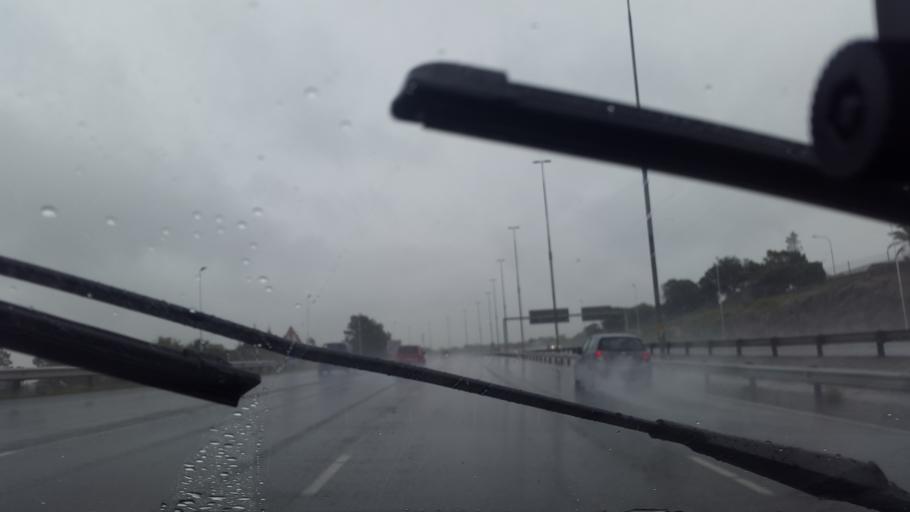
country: ZA
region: Gauteng
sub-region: City of Johannesburg Metropolitan Municipality
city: Johannesburg
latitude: -26.2611
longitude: 28.0055
